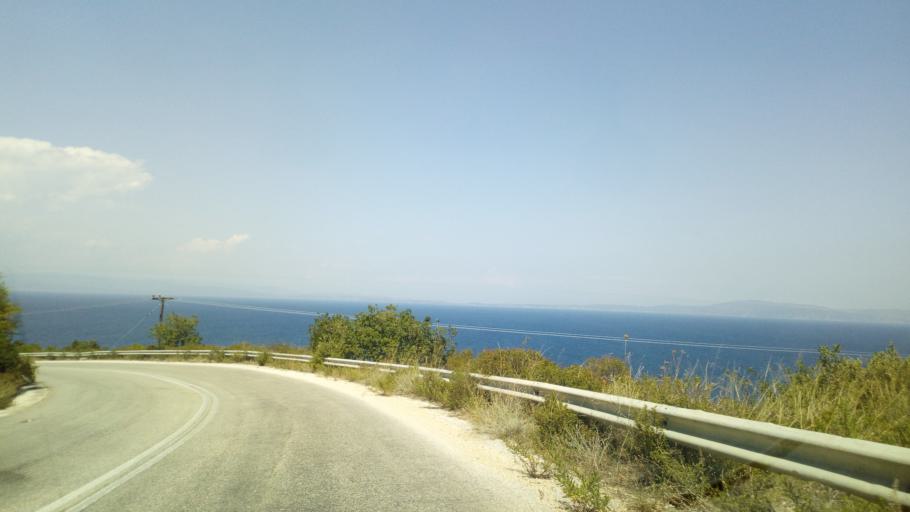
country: GR
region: Central Macedonia
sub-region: Nomos Chalkidikis
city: Sarti
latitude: 40.1577
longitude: 23.9012
